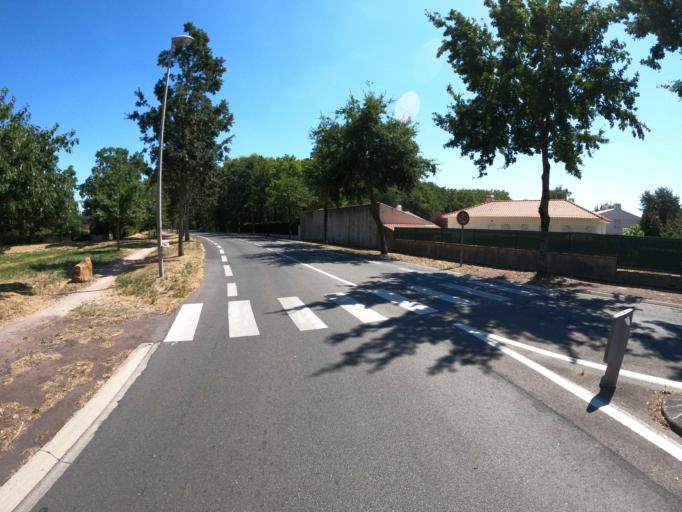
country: FR
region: Pays de la Loire
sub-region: Departement de la Vendee
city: Challans
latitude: 46.8395
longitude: -1.8931
